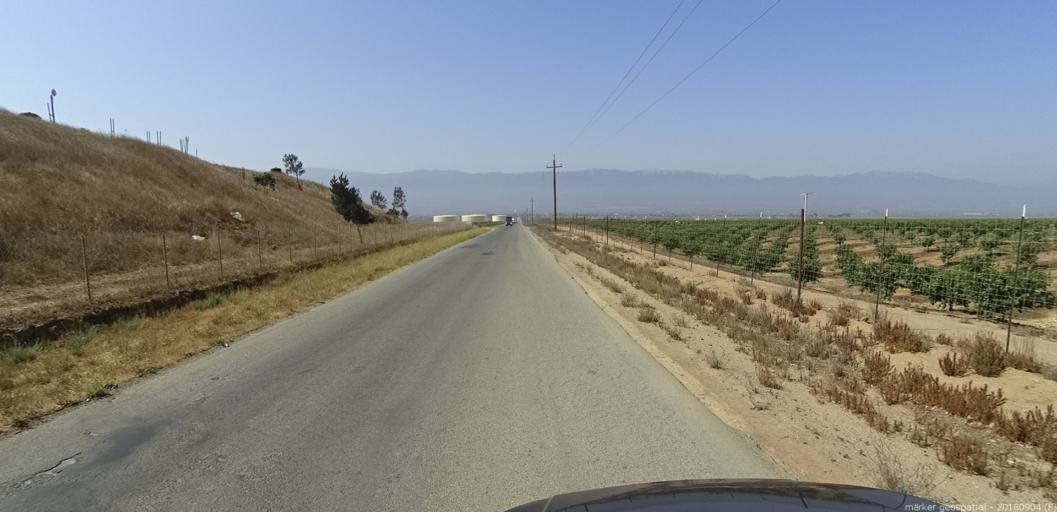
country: US
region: California
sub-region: Monterey County
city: Gonzales
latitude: 36.5311
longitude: -121.4112
